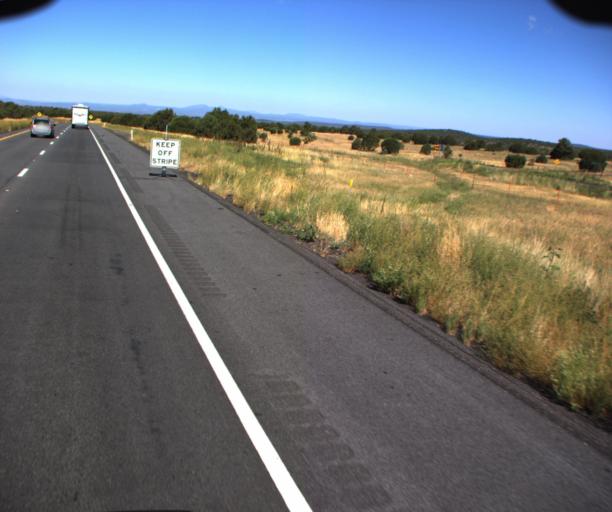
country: US
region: Arizona
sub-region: Coconino County
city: Williams
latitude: 35.2225
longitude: -112.3189
